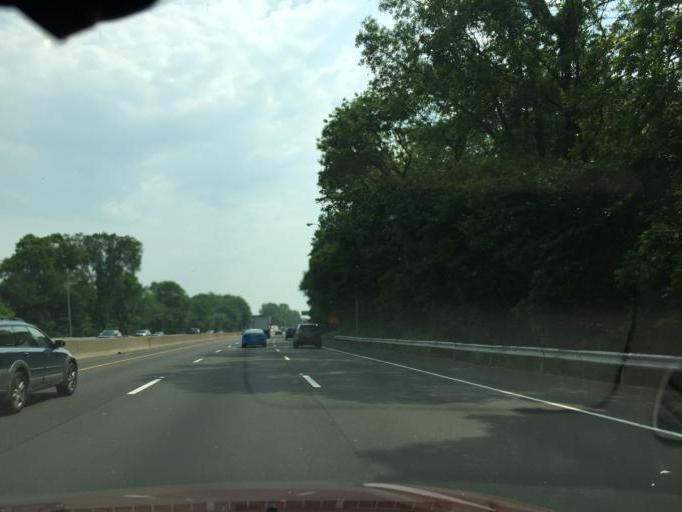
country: US
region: Connecticut
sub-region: Fairfield County
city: Cos Cob
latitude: 41.0247
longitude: -73.6117
